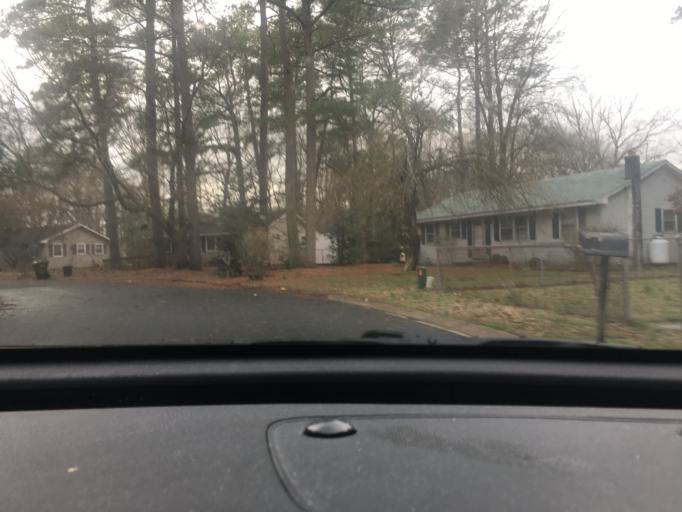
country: US
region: Maryland
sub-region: Wicomico County
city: Salisbury
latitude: 38.3805
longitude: -75.6134
